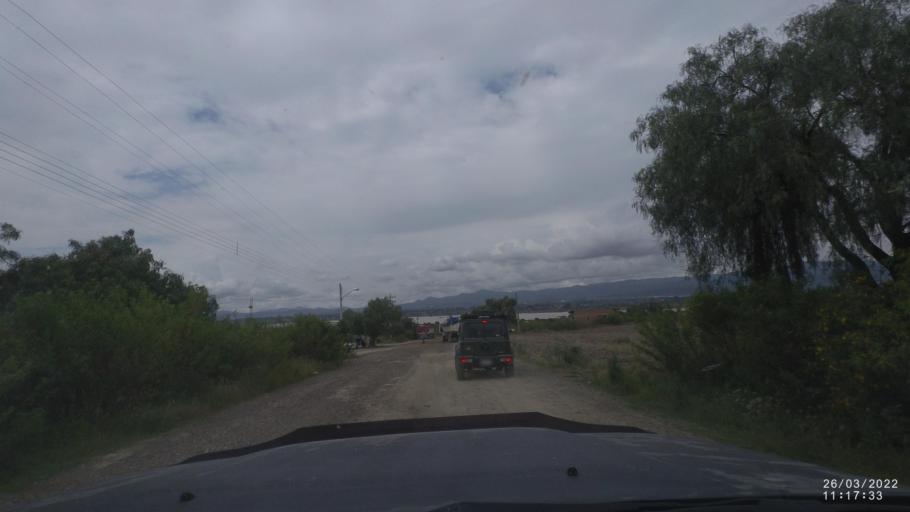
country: BO
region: Cochabamba
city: Tarata
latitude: -17.5398
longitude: -66.0228
